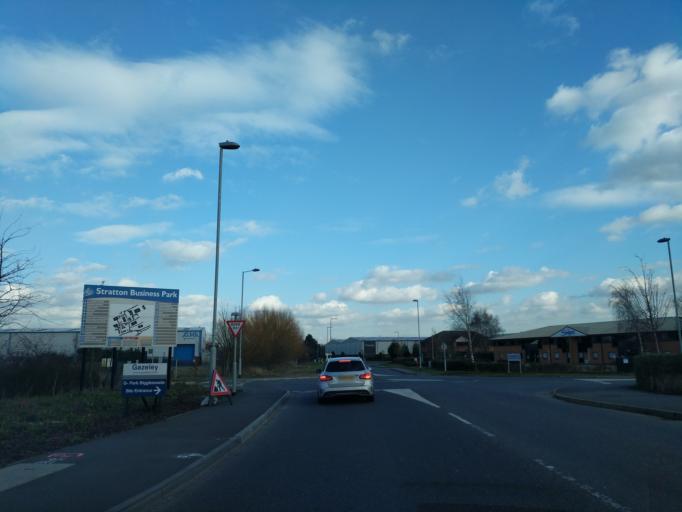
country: GB
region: England
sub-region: Central Bedfordshire
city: Biggleswade
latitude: 52.0735
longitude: -0.2422
